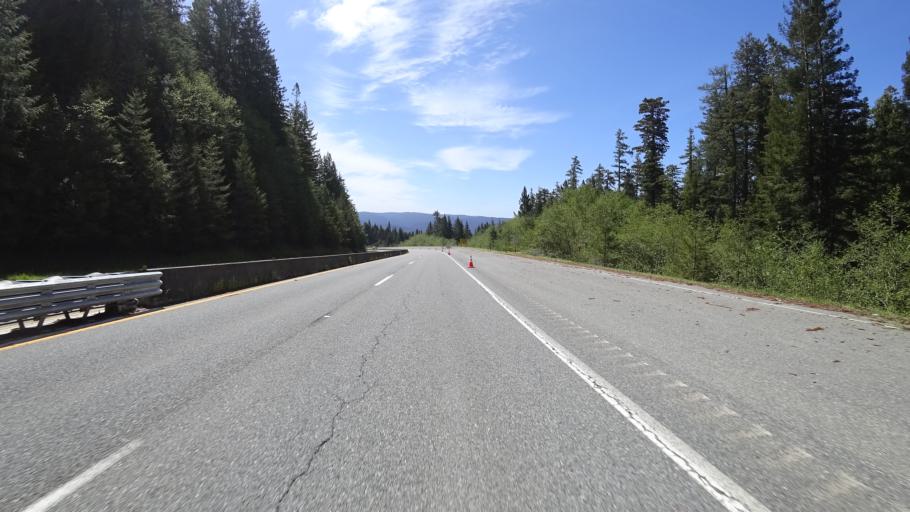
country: US
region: California
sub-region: Humboldt County
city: Westhaven-Moonstone
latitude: 41.3792
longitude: -123.9953
